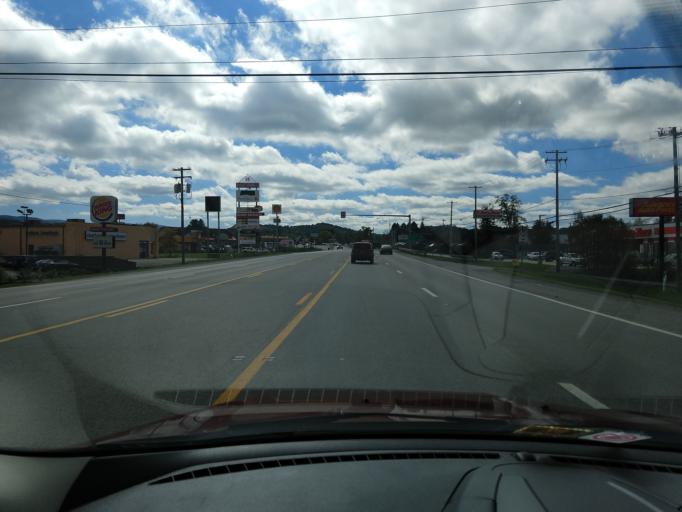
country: US
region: West Virginia
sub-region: Randolph County
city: Elkins
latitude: 38.8927
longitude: -79.8465
